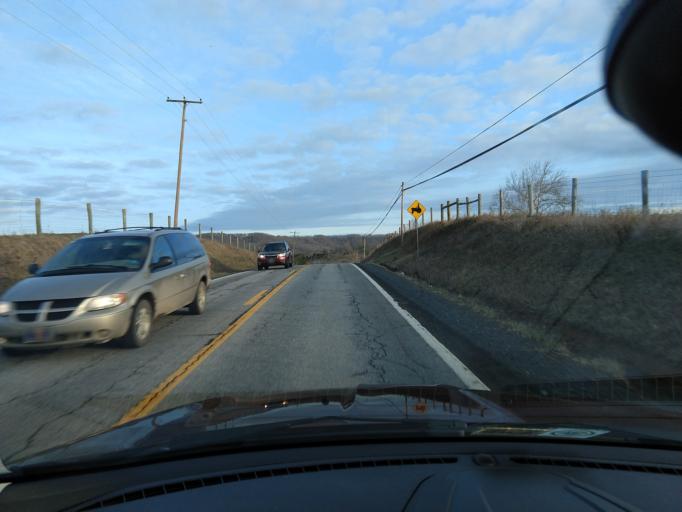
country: US
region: West Virginia
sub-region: Greenbrier County
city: Lewisburg
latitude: 37.9688
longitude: -80.3828
